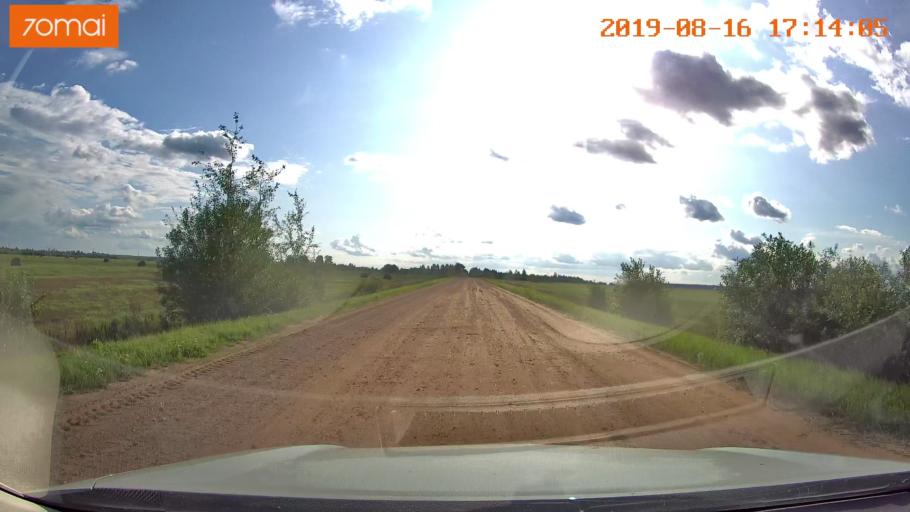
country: BY
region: Mogilev
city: Hlusha
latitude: 53.1860
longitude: 28.8648
